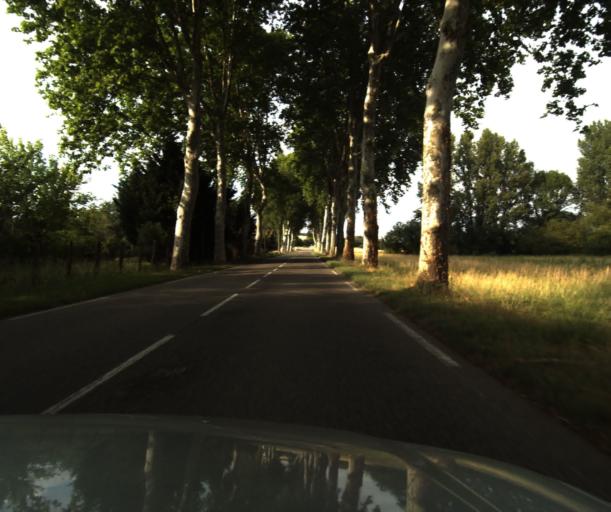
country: FR
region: Midi-Pyrenees
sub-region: Departement du Tarn-et-Garonne
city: Beaumont-de-Lomagne
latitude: 43.8552
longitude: 0.9449
